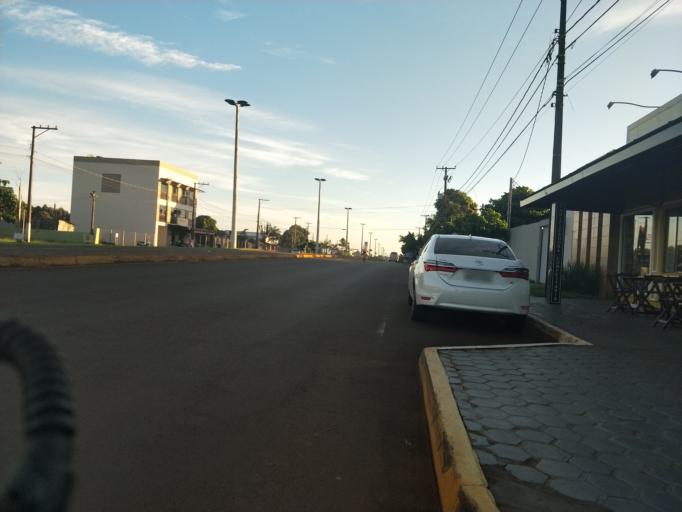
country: BR
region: Parana
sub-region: Marechal Candido Rondon
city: Marechal Candido Rondon
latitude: -24.5602
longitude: -54.0492
